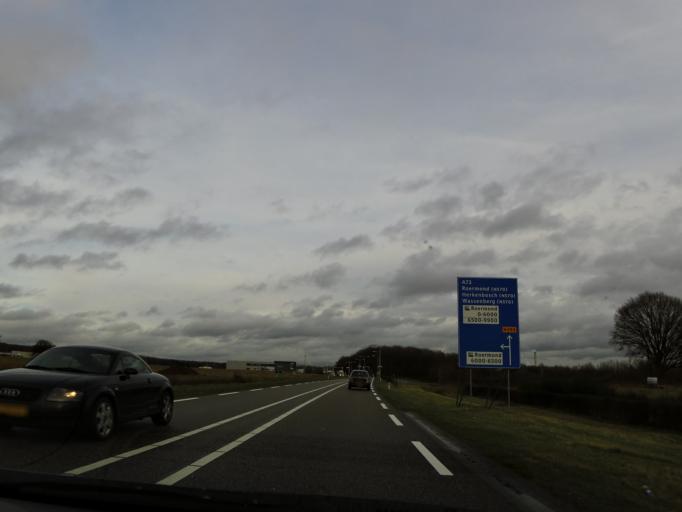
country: NL
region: Limburg
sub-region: Gemeente Roerdalen
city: Melick
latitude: 51.1698
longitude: 6.0190
